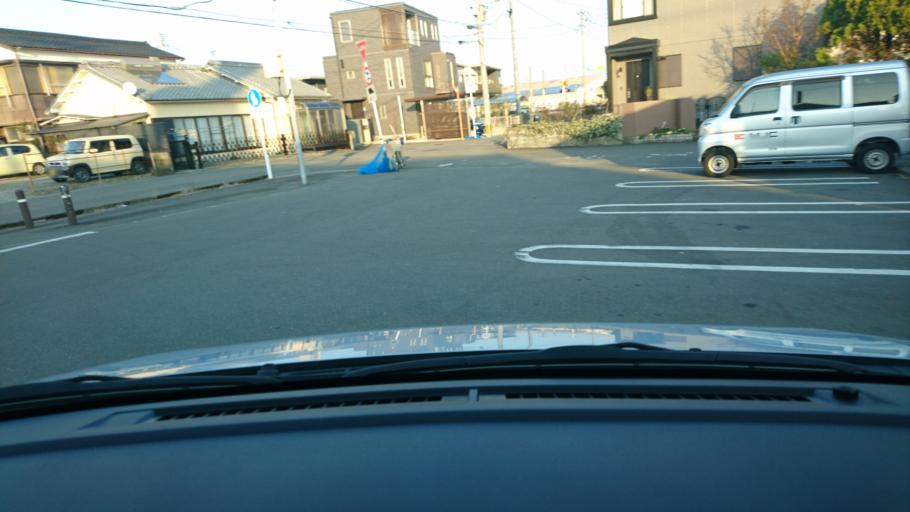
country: JP
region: Miyazaki
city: Miyazaki-shi
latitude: 31.9436
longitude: 131.4317
